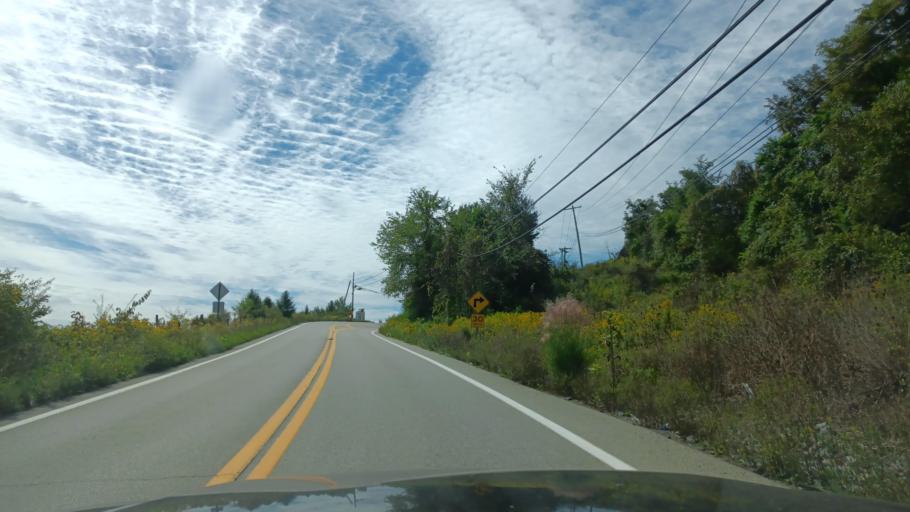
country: US
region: West Virginia
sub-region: Harrison County
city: Bridgeport
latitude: 39.2949
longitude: -80.2147
